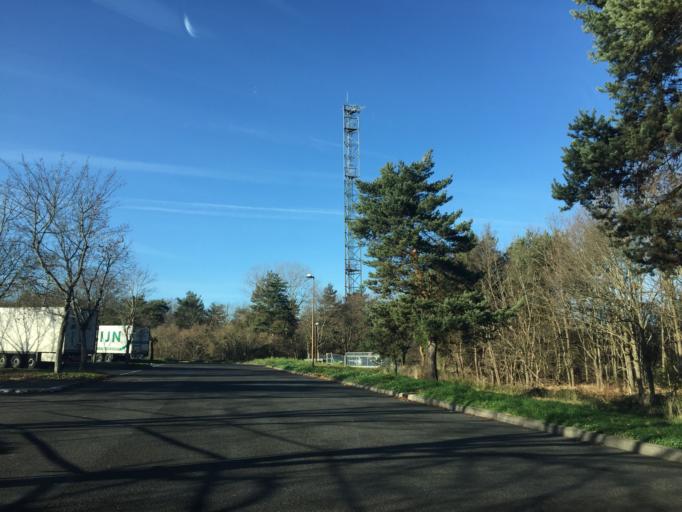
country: FR
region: Auvergne
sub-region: Departement du Puy-de-Dome
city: Orleat
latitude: 45.8526
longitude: 3.4047
